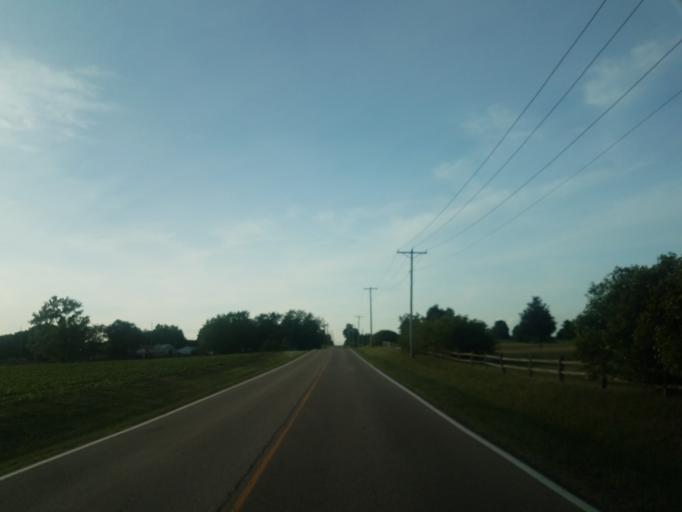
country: US
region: Illinois
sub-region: McLean County
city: Bloomington
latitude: 40.4421
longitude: -89.0054
